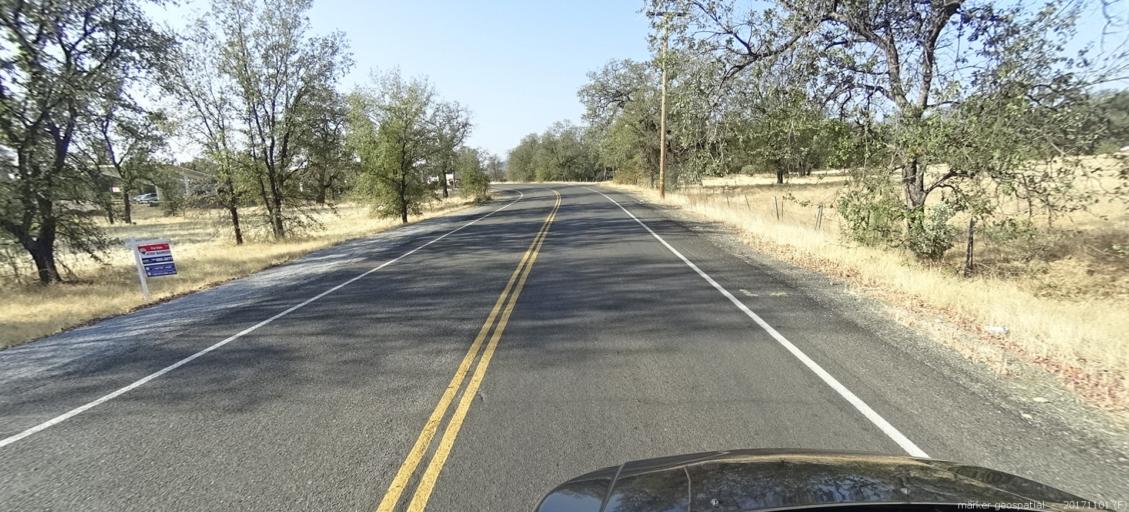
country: US
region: California
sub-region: Shasta County
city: Shasta Lake
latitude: 40.7078
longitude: -122.3374
